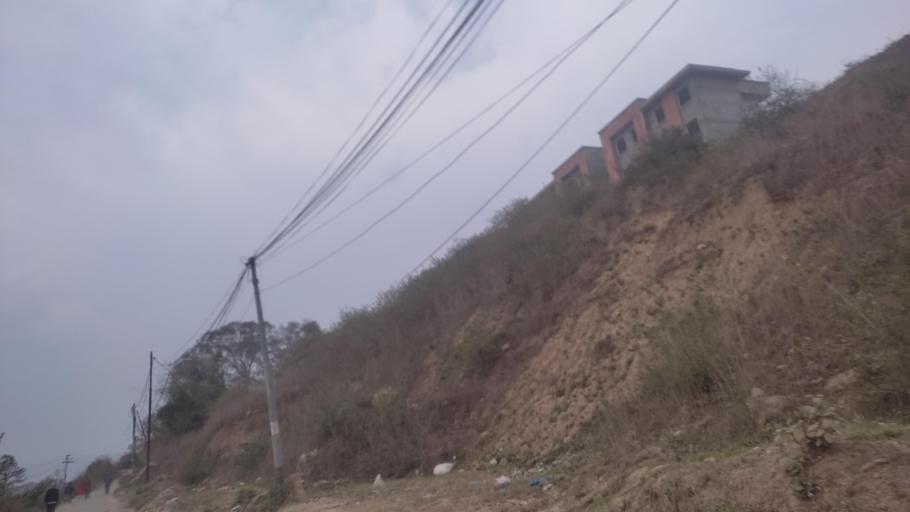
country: NP
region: Central Region
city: Kirtipur
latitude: 27.6642
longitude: 85.2872
